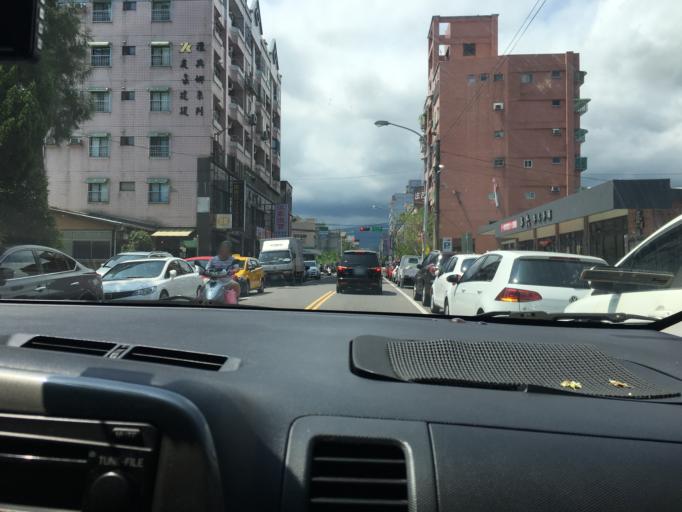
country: TW
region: Taiwan
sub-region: Yilan
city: Yilan
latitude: 24.7454
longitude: 121.7432
